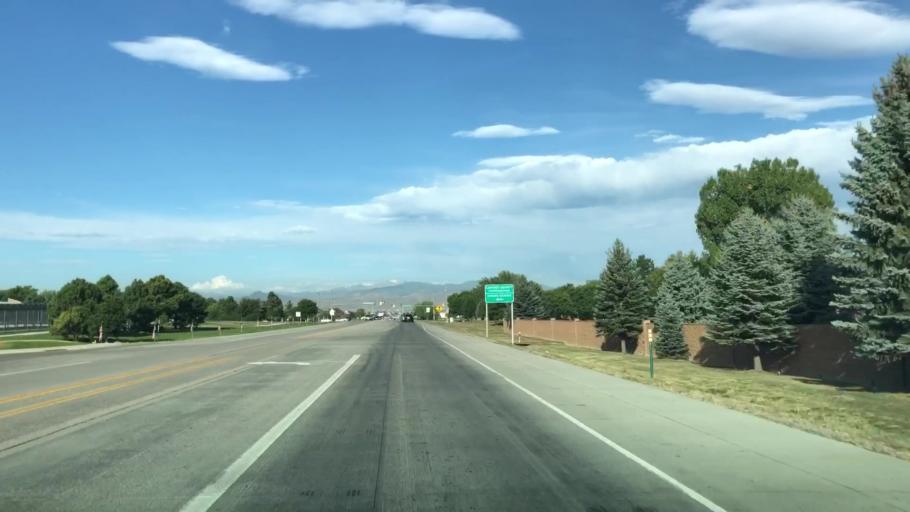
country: US
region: Colorado
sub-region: Weld County
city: Windsor
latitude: 40.4795
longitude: -104.9783
